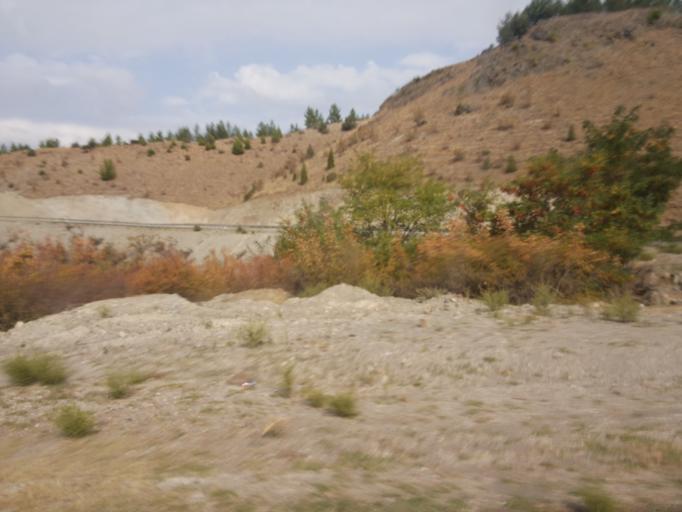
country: TR
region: Corum
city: Kamil
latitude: 41.1060
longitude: 34.7423
